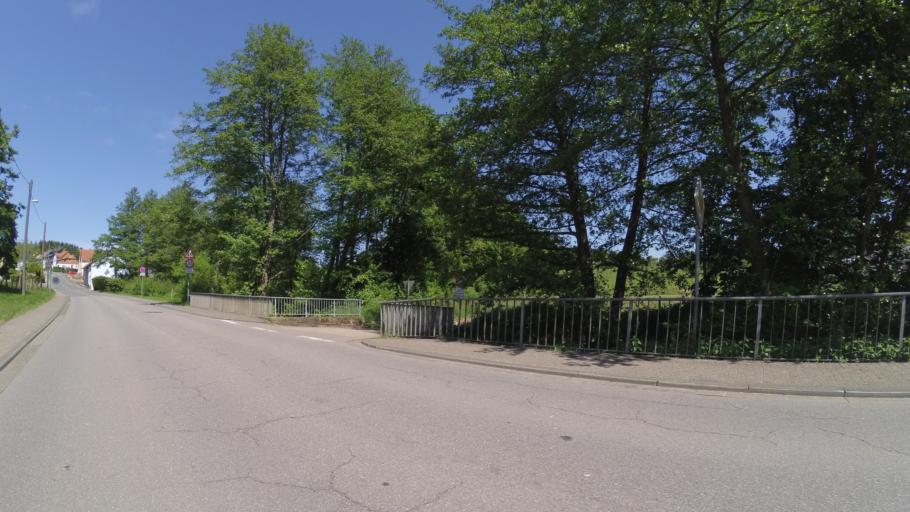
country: DE
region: Saarland
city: Heusweiler
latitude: 49.3615
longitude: 6.9368
